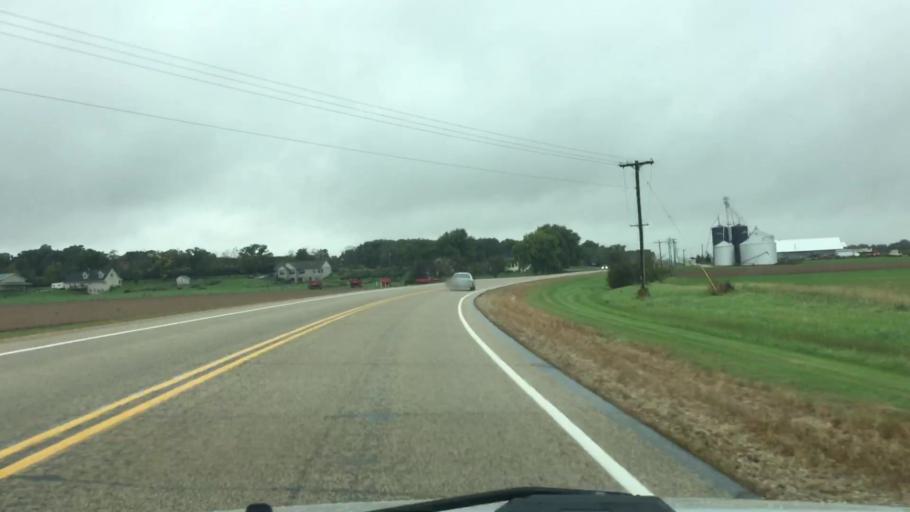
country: US
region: Wisconsin
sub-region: Walworth County
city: Whitewater
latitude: 42.8573
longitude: -88.6648
